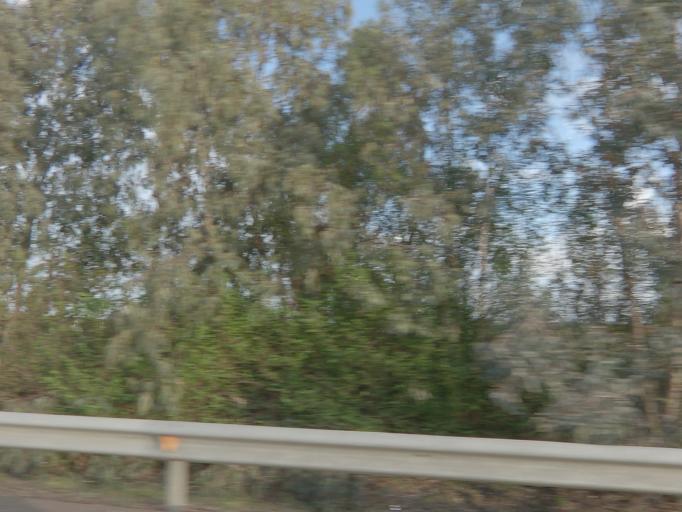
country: ES
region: Extremadura
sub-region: Provincia de Badajoz
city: Calamonte
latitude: 38.9027
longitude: -6.4052
